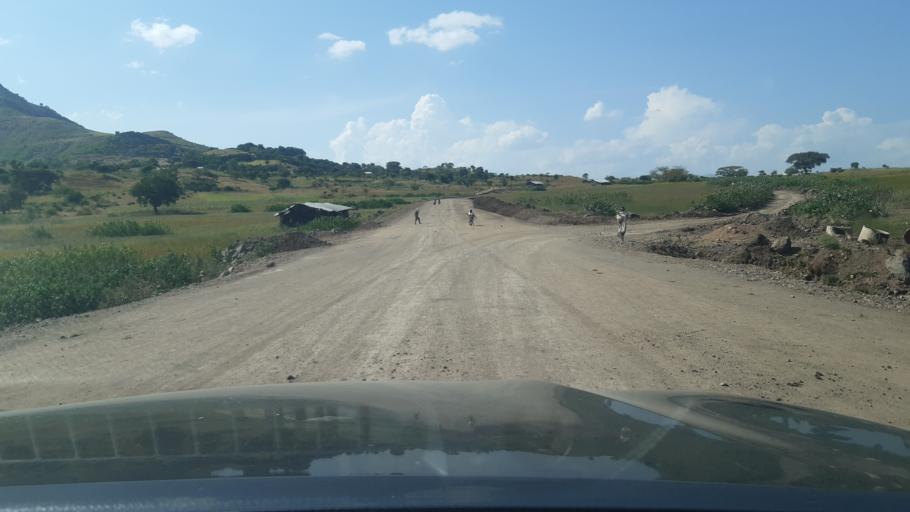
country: ET
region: Amhara
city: Dabat
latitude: 13.1580
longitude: 37.6104
